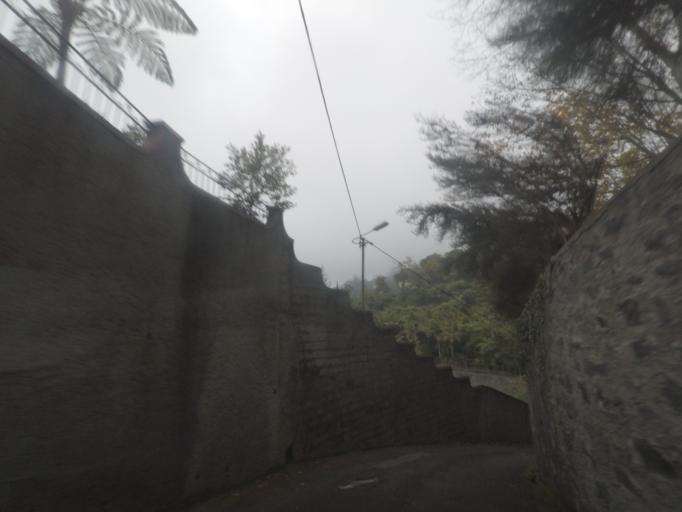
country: PT
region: Madeira
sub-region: Funchal
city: Nossa Senhora do Monte
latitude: 32.6725
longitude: -16.9022
